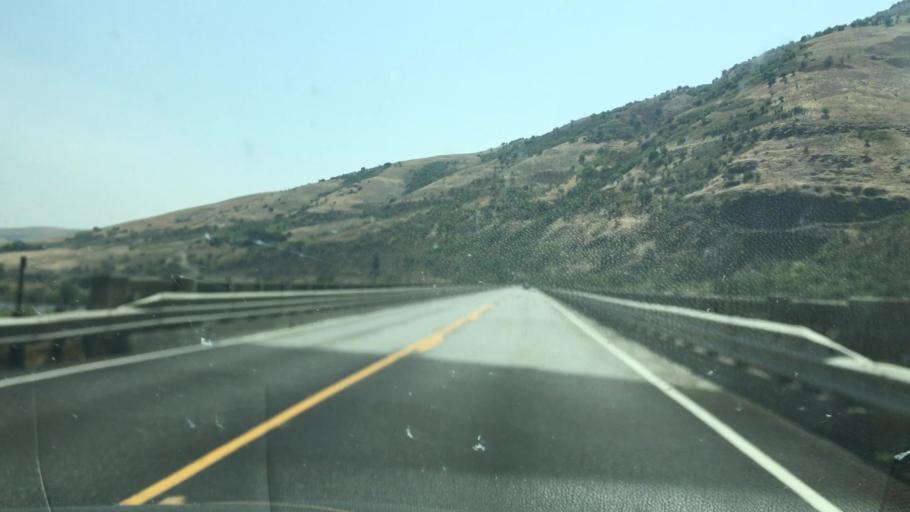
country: US
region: Idaho
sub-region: Nez Perce County
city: Lapwai
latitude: 46.4438
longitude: -116.8479
